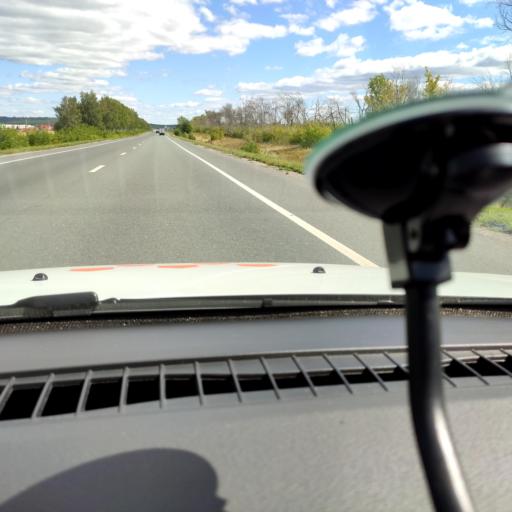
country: RU
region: Samara
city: Kurumoch
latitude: 53.4875
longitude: 50.0035
